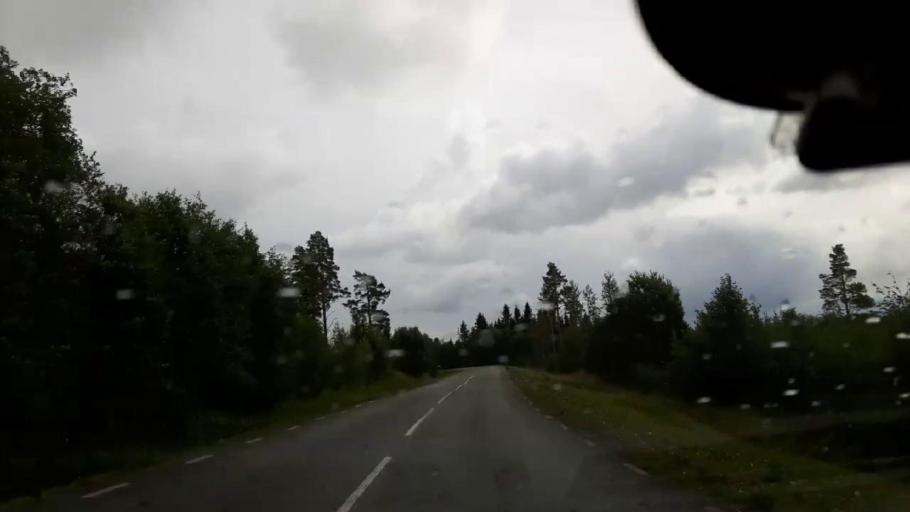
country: SE
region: Jaemtland
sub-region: Krokoms Kommun
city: Valla
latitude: 63.4132
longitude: 13.8058
